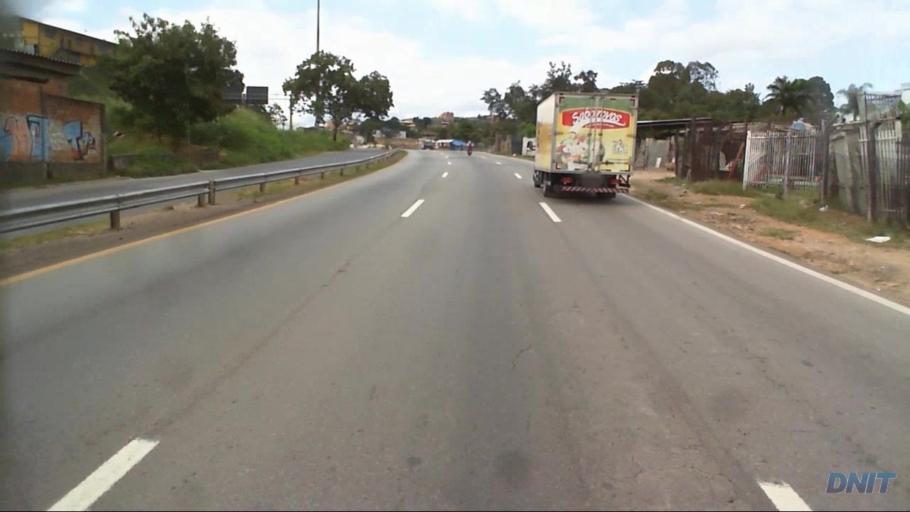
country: BR
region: Minas Gerais
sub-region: Belo Horizonte
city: Belo Horizonte
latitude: -19.8556
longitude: -43.8927
